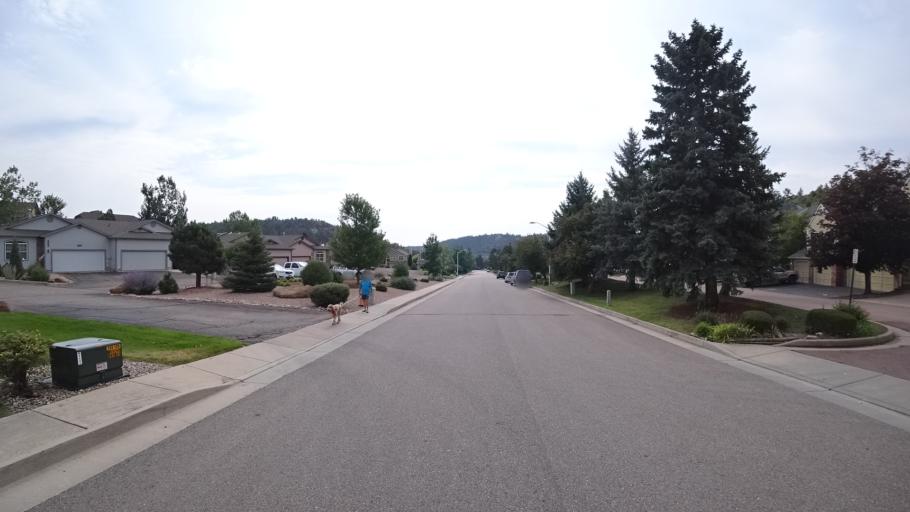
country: US
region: Colorado
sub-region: El Paso County
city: Colorado Springs
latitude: 38.8945
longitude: -104.7900
